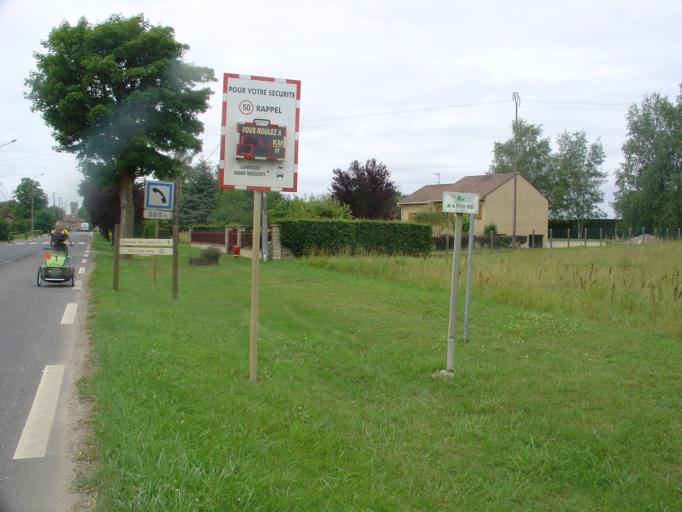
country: FR
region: Lorraine
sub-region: Departement de la Meuse
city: Vigneulles-les-Hattonchatel
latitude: 48.8538
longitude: 5.7924
